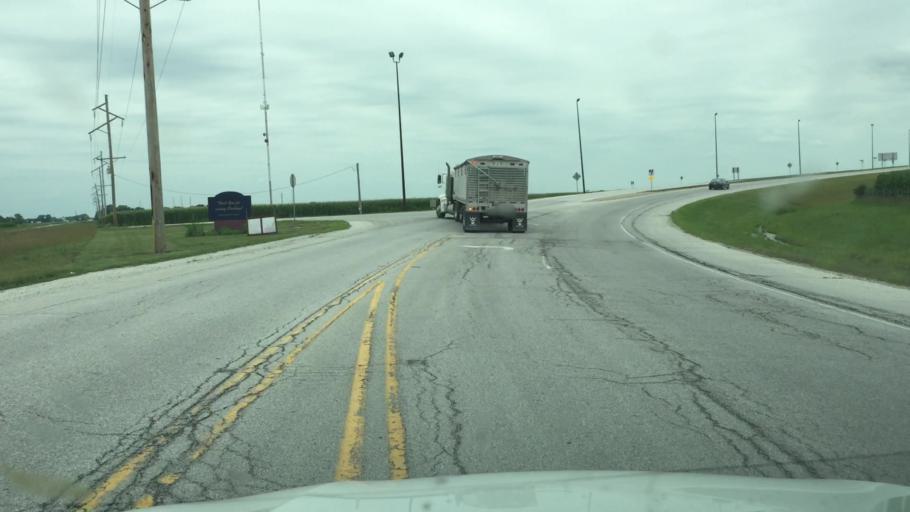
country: US
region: Illinois
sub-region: Hancock County
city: Carthage
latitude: 40.4158
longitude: -91.1163
